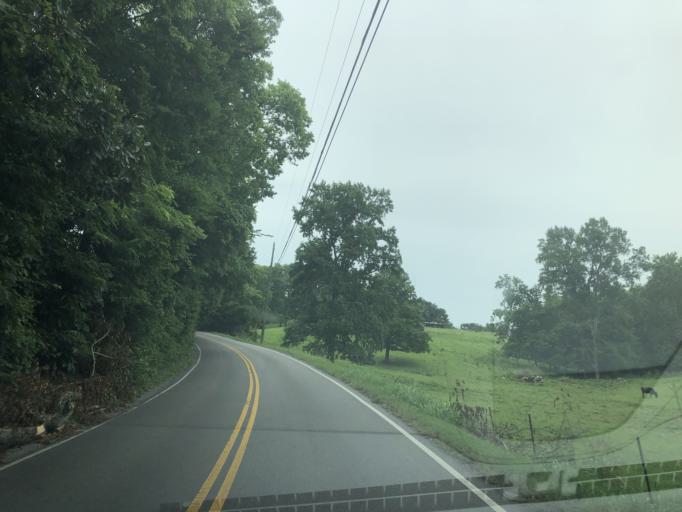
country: US
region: Tennessee
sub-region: Williamson County
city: Nolensville
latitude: 36.0343
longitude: -86.6939
